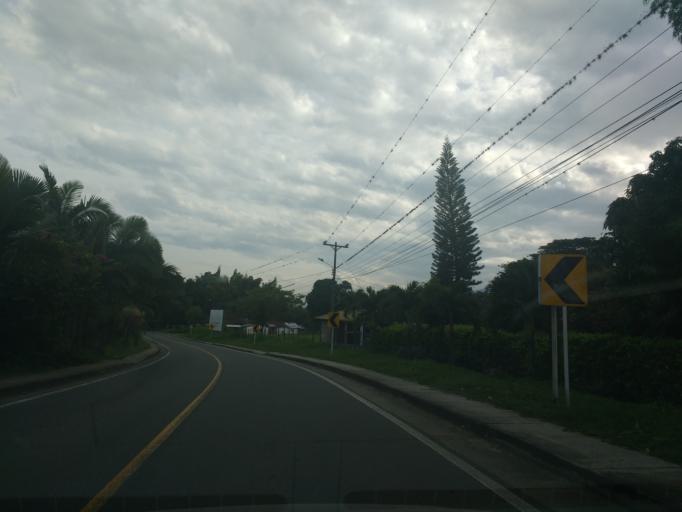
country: CO
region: Cauca
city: Miranda
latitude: 3.2772
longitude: -76.2214
